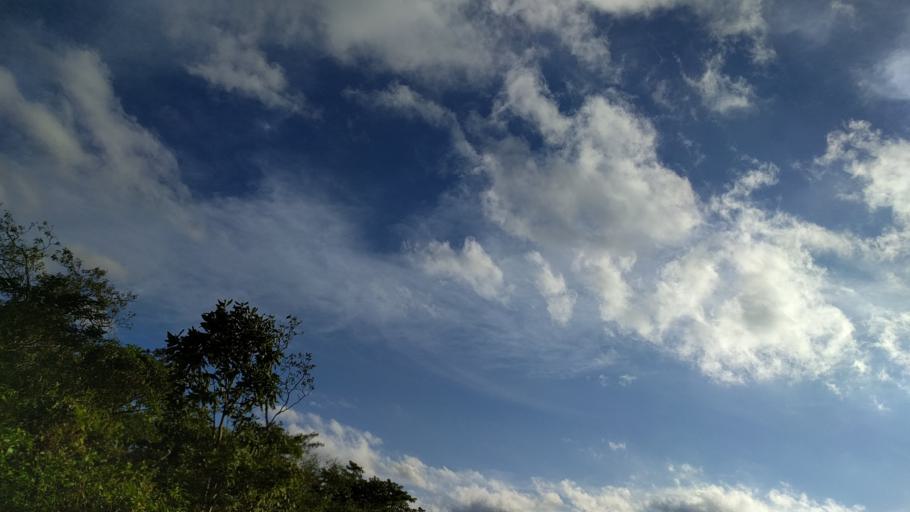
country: BO
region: Santa Cruz
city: Santa Rita
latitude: -17.8497
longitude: -63.2944
